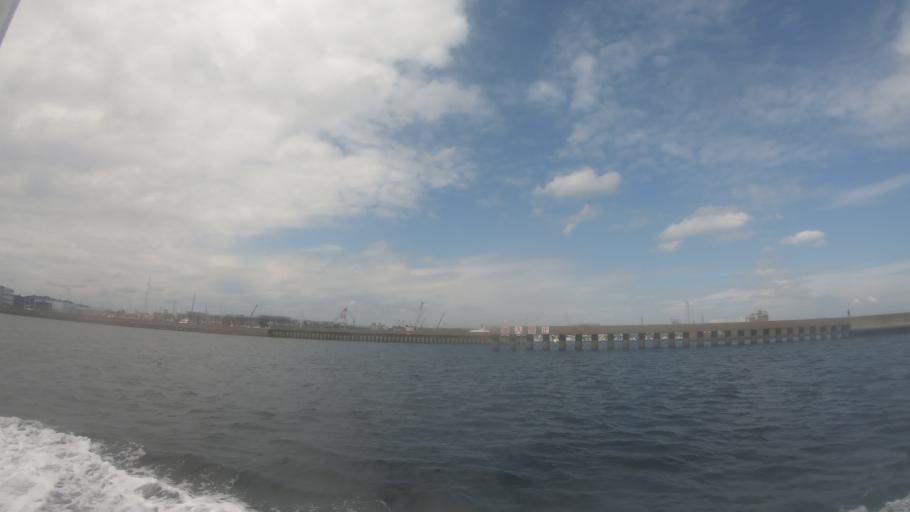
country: JP
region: Kanagawa
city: Yokohama
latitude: 35.3782
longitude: 139.6541
